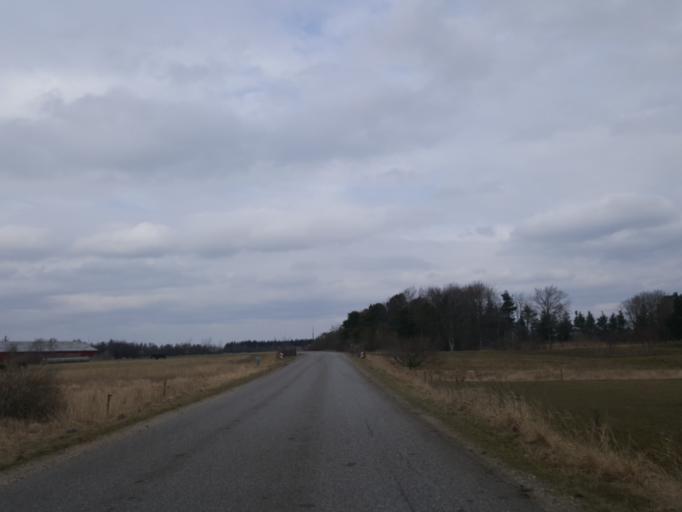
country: DK
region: Central Jutland
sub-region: Holstebro Kommune
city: Ulfborg
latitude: 56.3466
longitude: 8.3041
